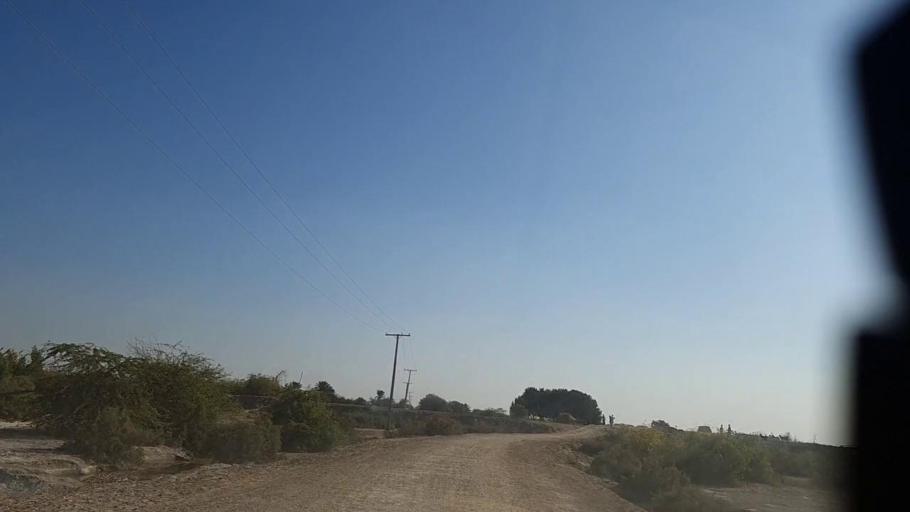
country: PK
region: Sindh
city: Digri
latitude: 25.1478
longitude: 69.0373
